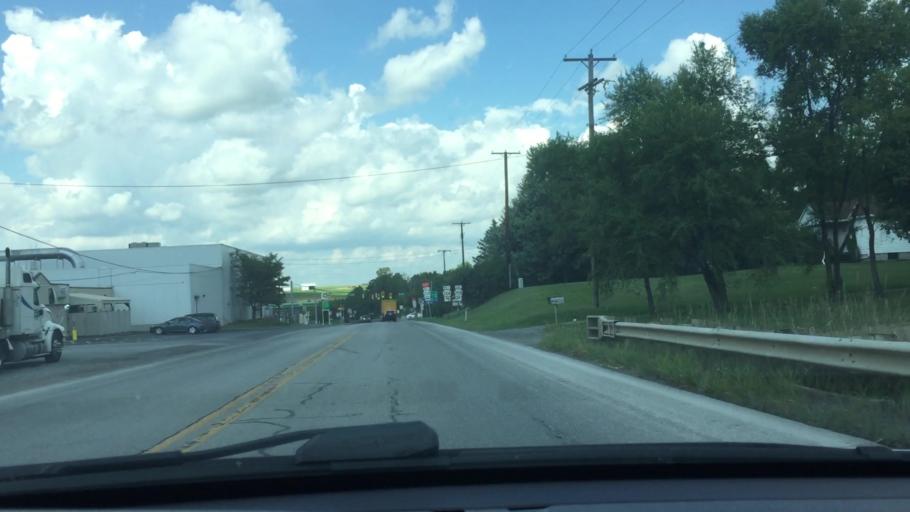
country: US
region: Pennsylvania
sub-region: Lawrence County
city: New Wilmington
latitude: 41.1188
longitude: -80.3597
